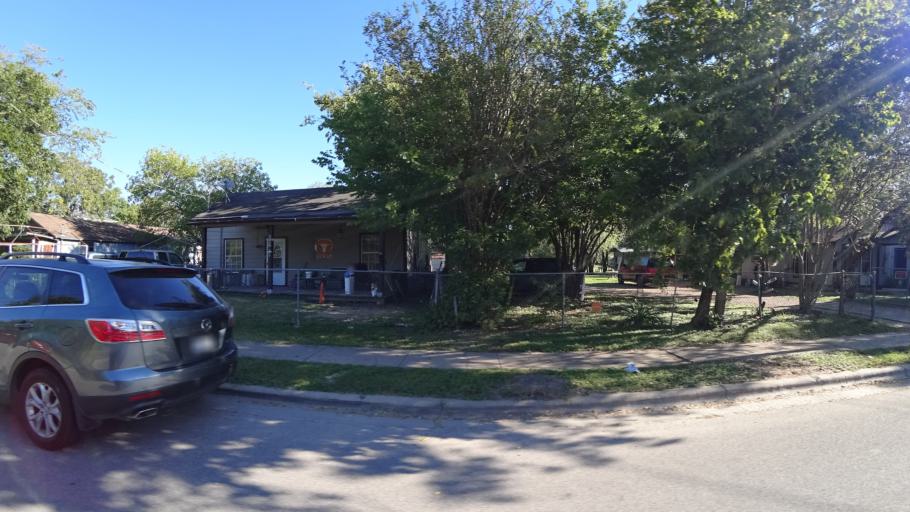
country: US
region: Texas
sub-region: Travis County
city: Austin
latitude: 30.2301
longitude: -97.6980
